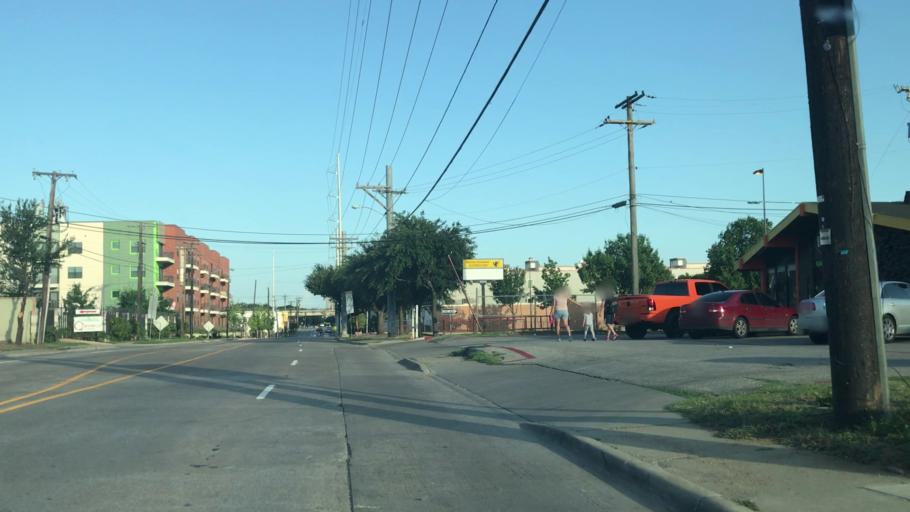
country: US
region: Texas
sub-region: Dallas County
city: Highland Park
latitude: 32.8209
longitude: -96.8361
